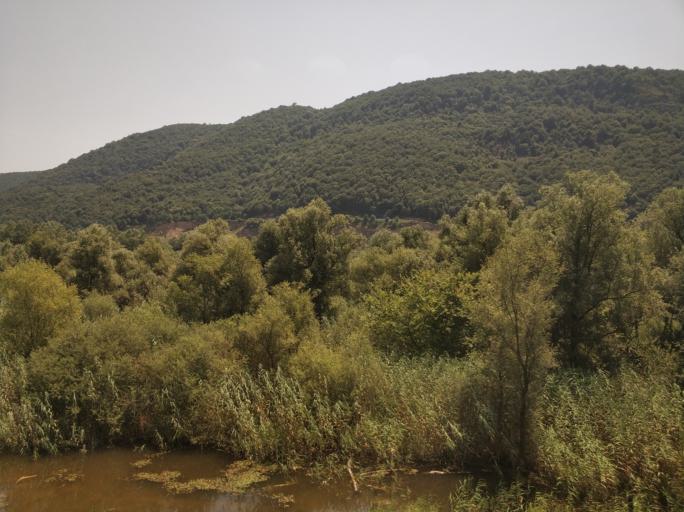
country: IR
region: Gilan
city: Pa'in-e Bazar-e Rudbar
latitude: 36.9833
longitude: 49.5576
